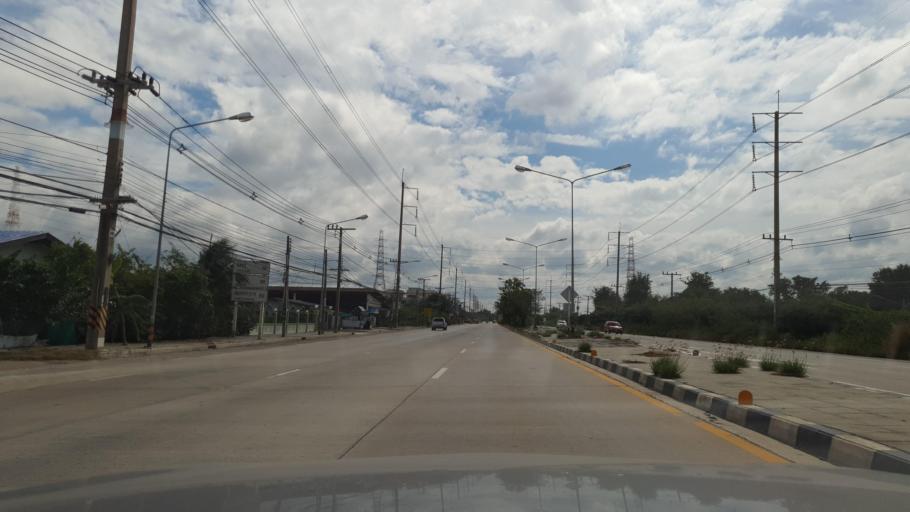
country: TH
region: Chachoengsao
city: Bang Pakong
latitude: 13.5269
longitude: 100.9921
